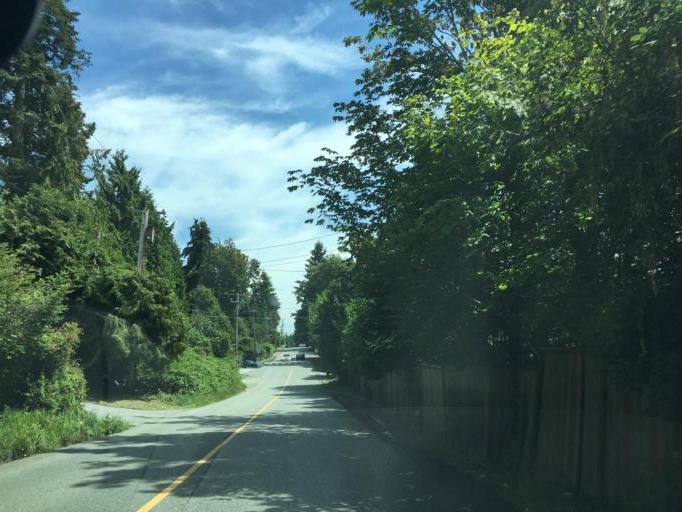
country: CA
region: British Columbia
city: West Vancouver
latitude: 49.3412
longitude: -123.2434
